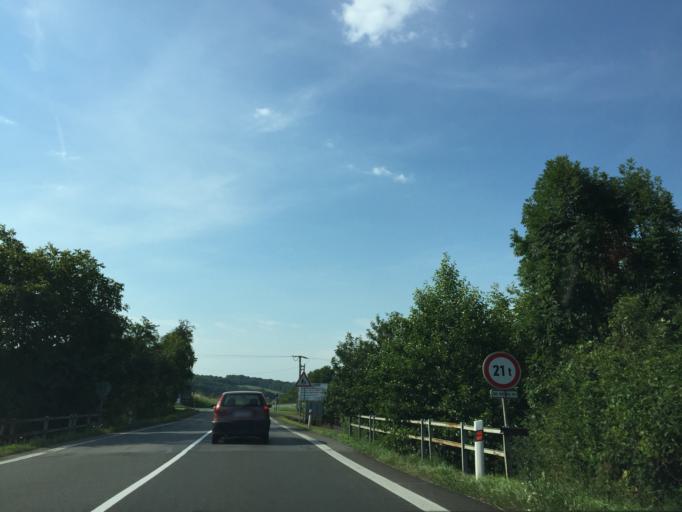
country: SK
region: Presovsky
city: Vranov nad Topl'ou
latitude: 48.9676
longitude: 21.5809
